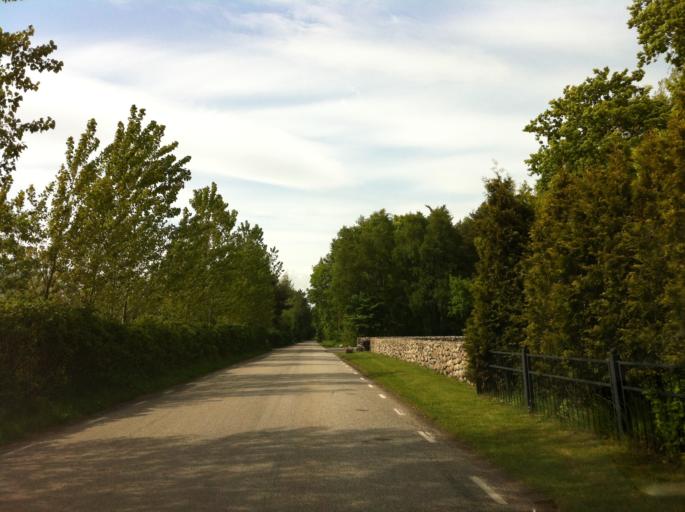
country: SE
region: Skane
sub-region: Landskrona
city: Asmundtorp
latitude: 55.8341
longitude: 12.9216
